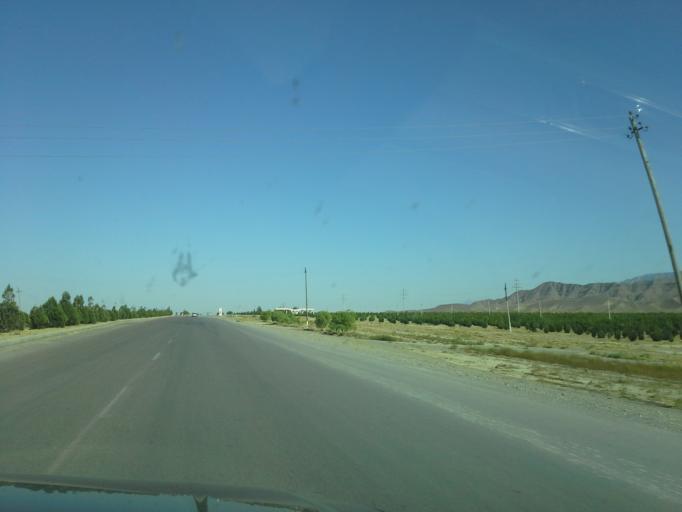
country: TM
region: Ahal
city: Baharly
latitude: 38.2775
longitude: 57.6798
